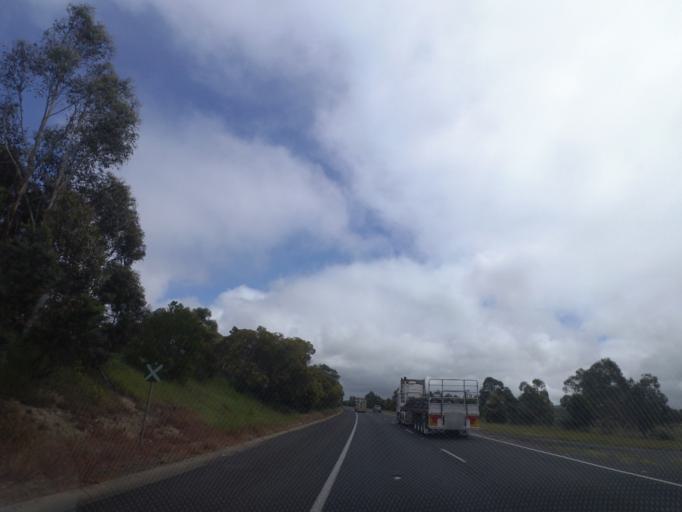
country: AU
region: Victoria
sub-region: Ballarat North
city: Soldiers Hill
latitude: -37.5223
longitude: 143.8606
